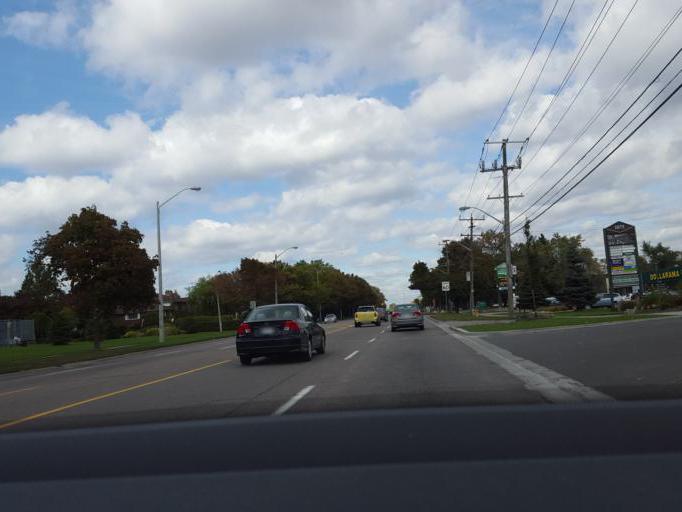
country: CA
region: Ontario
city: Willowdale
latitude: 43.7555
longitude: -79.3605
